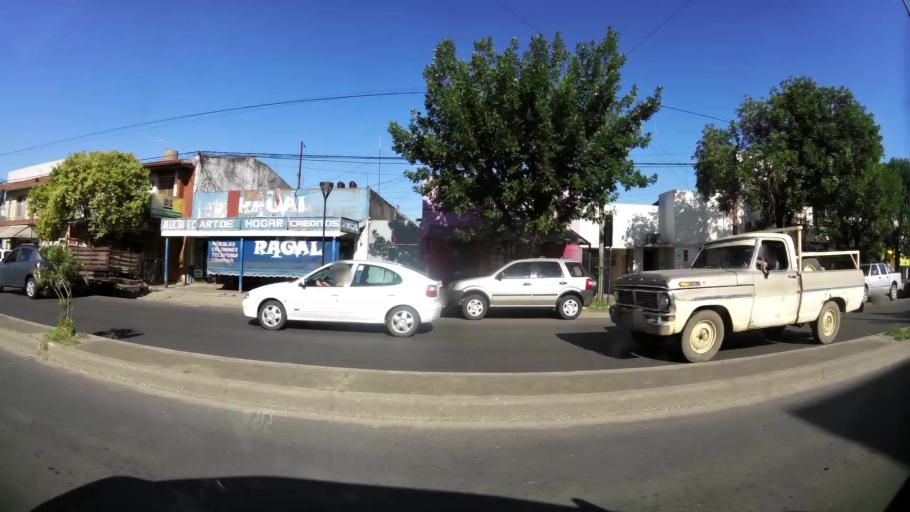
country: AR
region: Santa Fe
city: Santa Fe de la Vera Cruz
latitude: -31.6117
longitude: -60.7048
